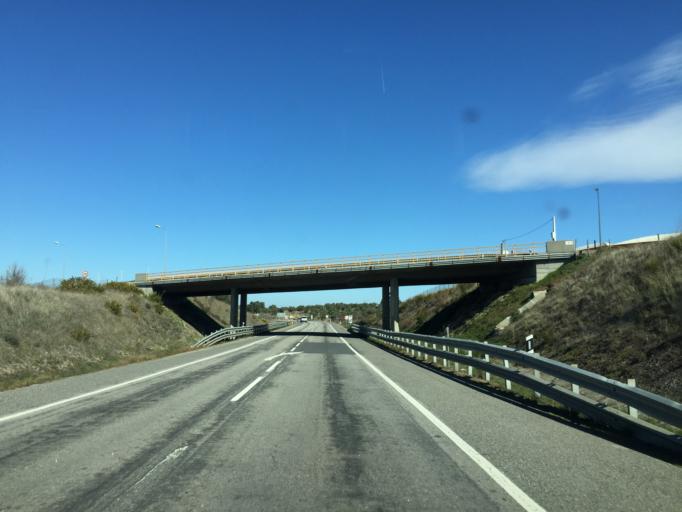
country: PT
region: Castelo Branco
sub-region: Castelo Branco
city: Castelo Branco
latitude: 39.8366
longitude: -7.5013
